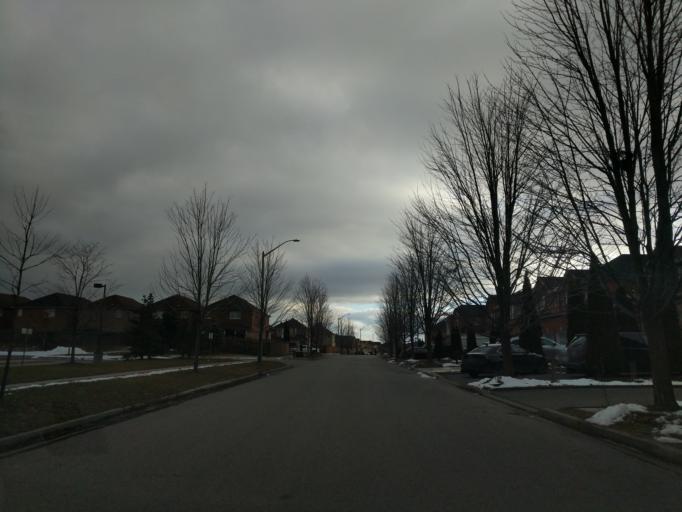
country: CA
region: Ontario
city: Markham
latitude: 43.8488
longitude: -79.2571
